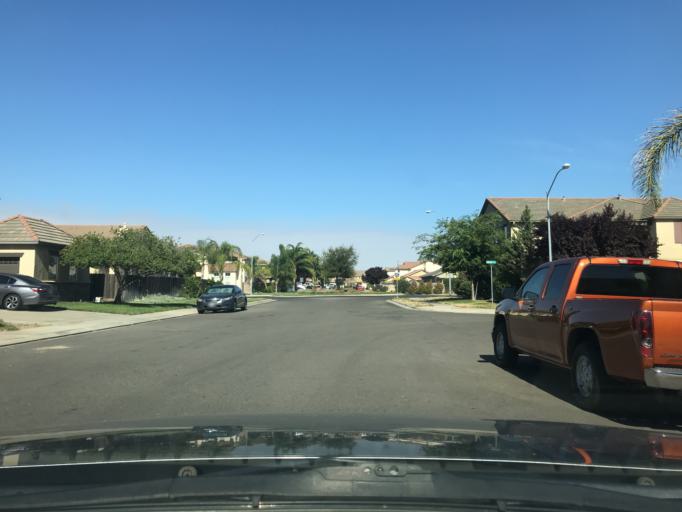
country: US
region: California
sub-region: Merced County
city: Atwater
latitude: 37.3437
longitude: -120.5736
